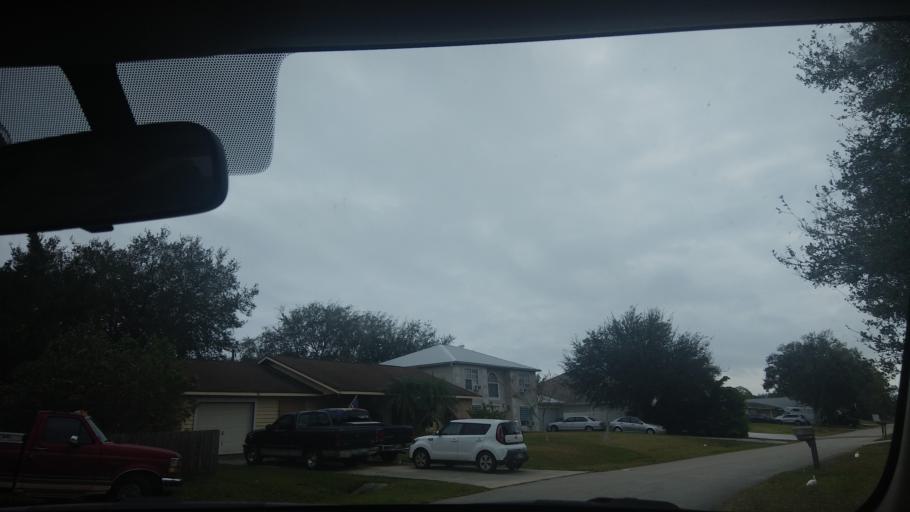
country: US
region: Florida
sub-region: Indian River County
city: Sebastian
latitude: 27.8054
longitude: -80.4903
